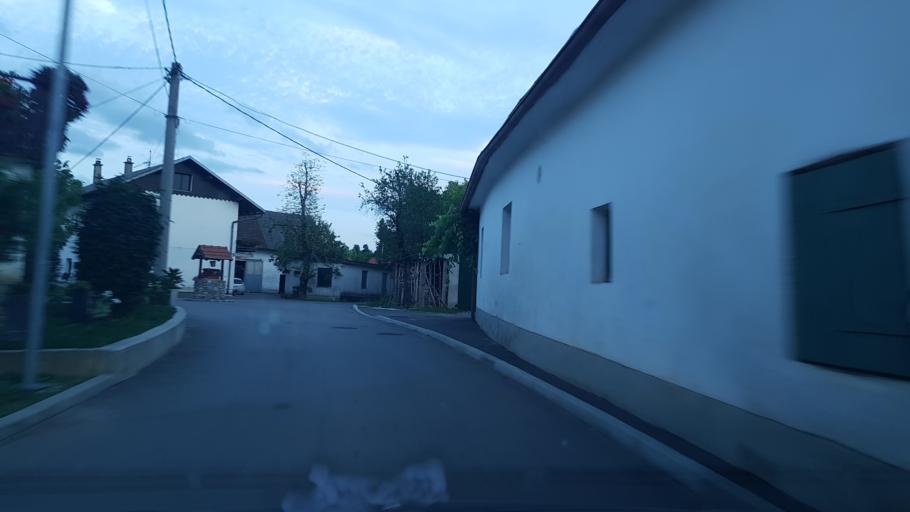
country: SI
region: Postojna
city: Postojna
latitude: 45.7504
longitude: 14.1789
